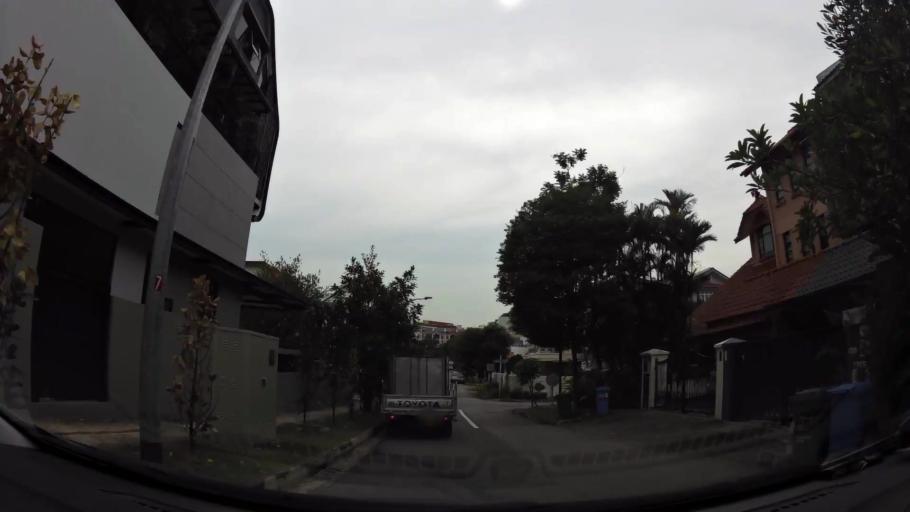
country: SG
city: Singapore
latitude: 1.3608
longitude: 103.8764
